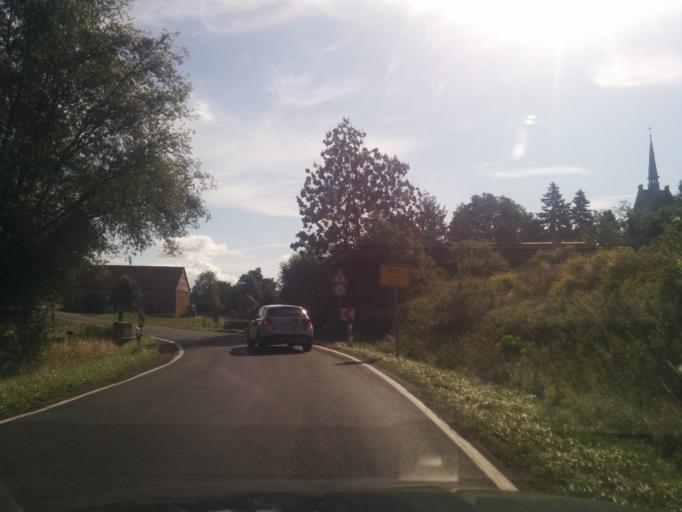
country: DE
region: Saxony-Anhalt
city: Schochwitz
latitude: 51.5293
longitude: 11.7790
